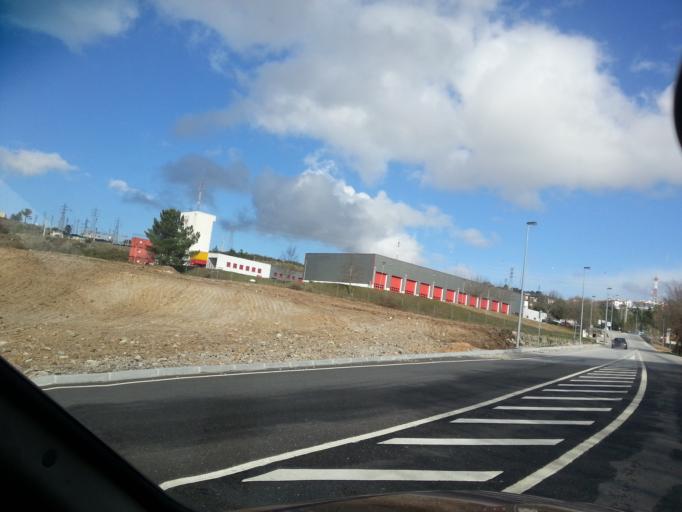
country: PT
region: Guarda
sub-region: Guarda
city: Guarda
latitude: 40.5352
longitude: -7.2922
